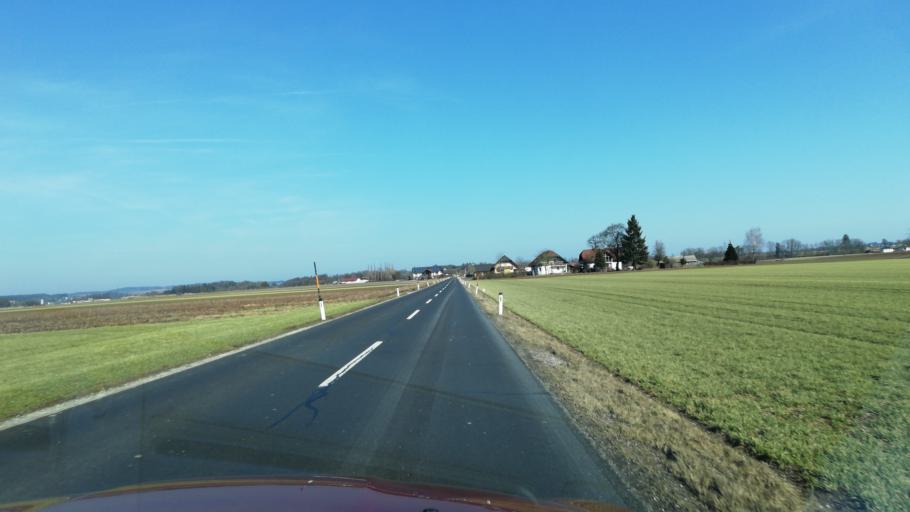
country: AT
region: Upper Austria
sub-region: Politischer Bezirk Vocklabruck
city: Desselbrunn
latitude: 48.0143
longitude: 13.7601
